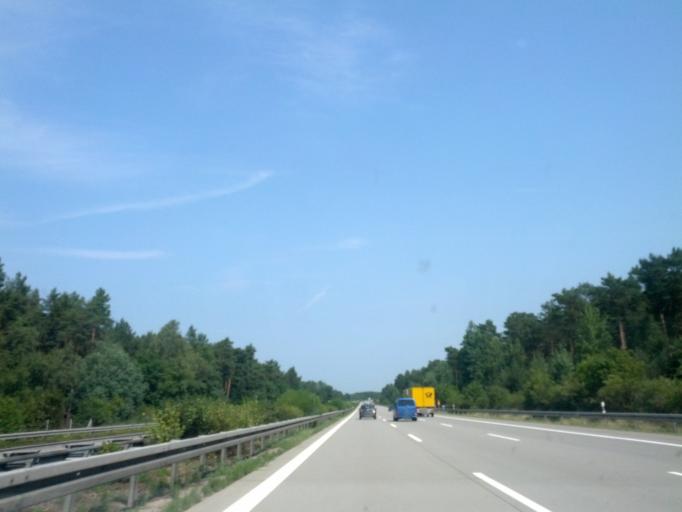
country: DE
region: Brandenburg
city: Niemegk
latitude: 52.1034
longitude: 12.7033
